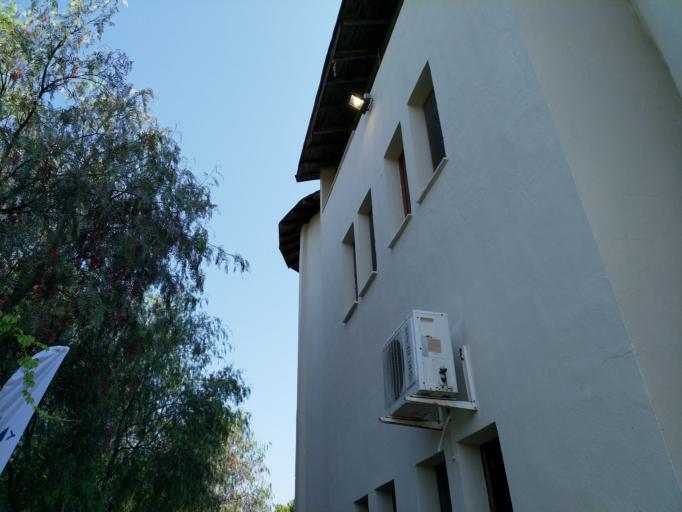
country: TR
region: Izmir
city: Urla
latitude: 38.3248
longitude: 26.7297
